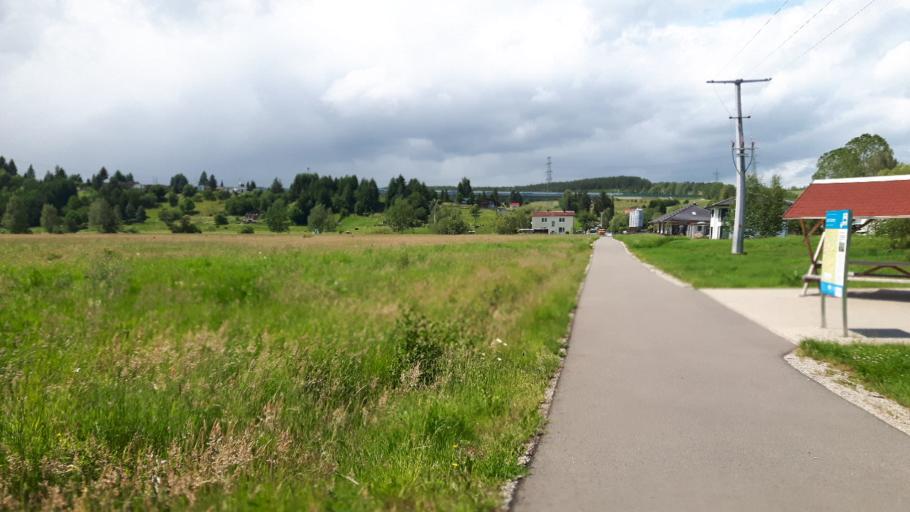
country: DE
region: Thuringia
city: Pennewitz
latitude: 50.6960
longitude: 11.0160
